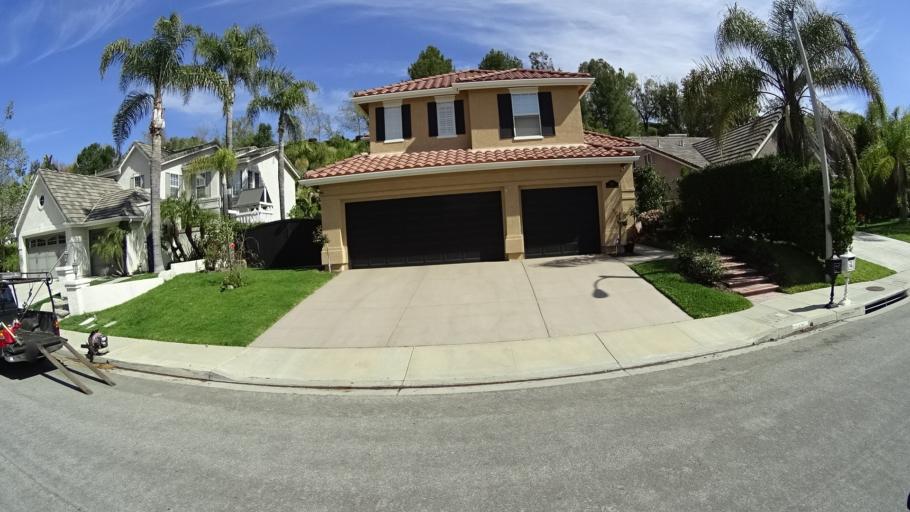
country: US
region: California
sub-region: Ventura County
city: Thousand Oaks
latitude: 34.2221
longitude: -118.8331
